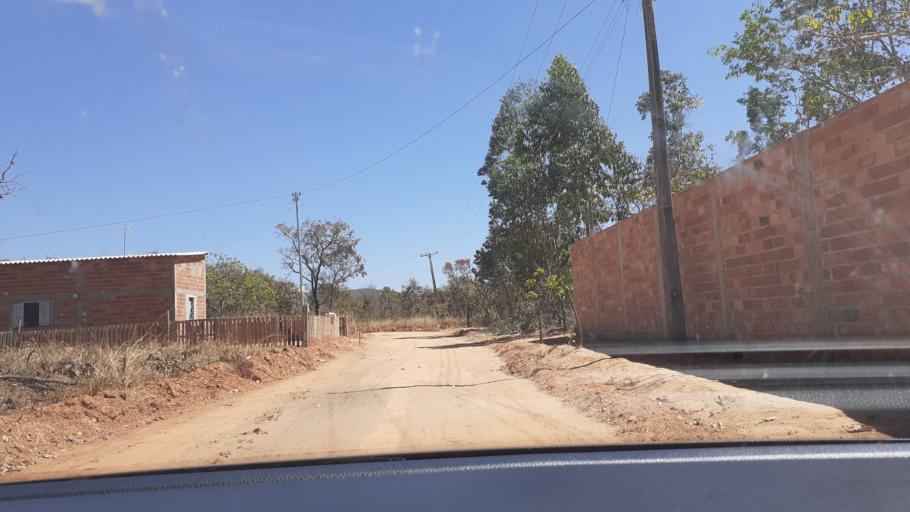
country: BR
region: Goias
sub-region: Caldas Novas
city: Caldas Novas
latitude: -17.7429
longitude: -48.6549
